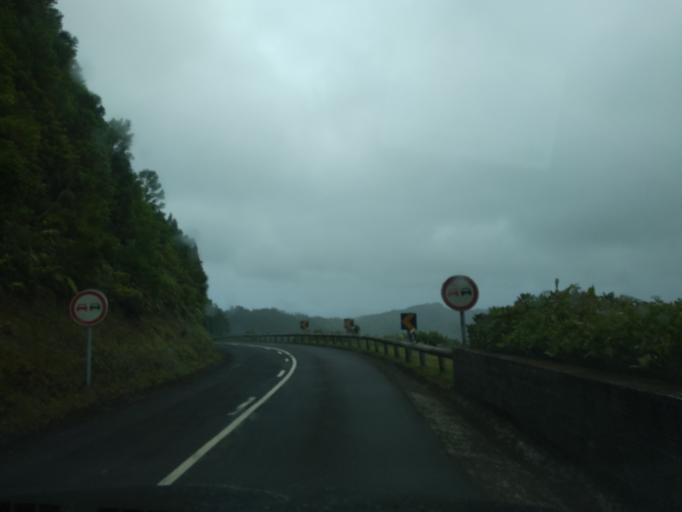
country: PT
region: Azores
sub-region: Ponta Delgada
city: Arrifes
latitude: 37.8387
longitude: -25.7893
